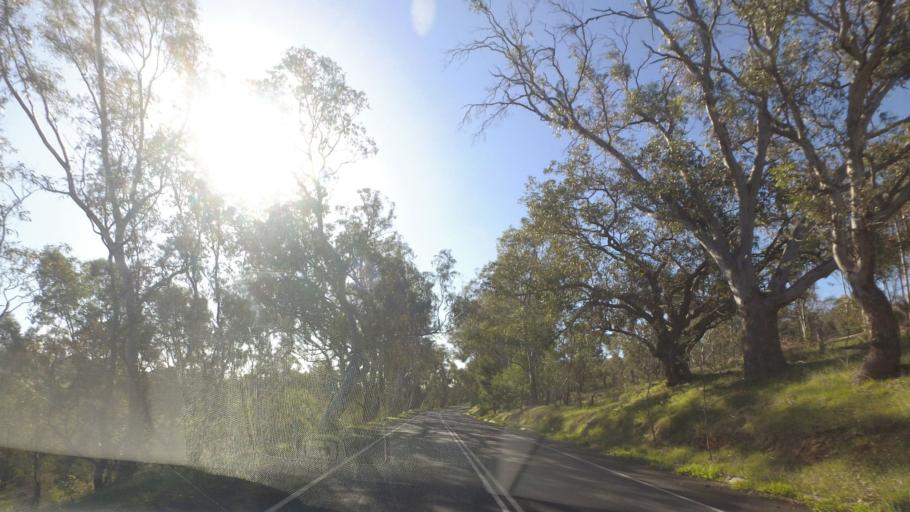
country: AU
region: Victoria
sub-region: Greater Bendigo
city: Kennington
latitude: -36.9440
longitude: 144.3386
